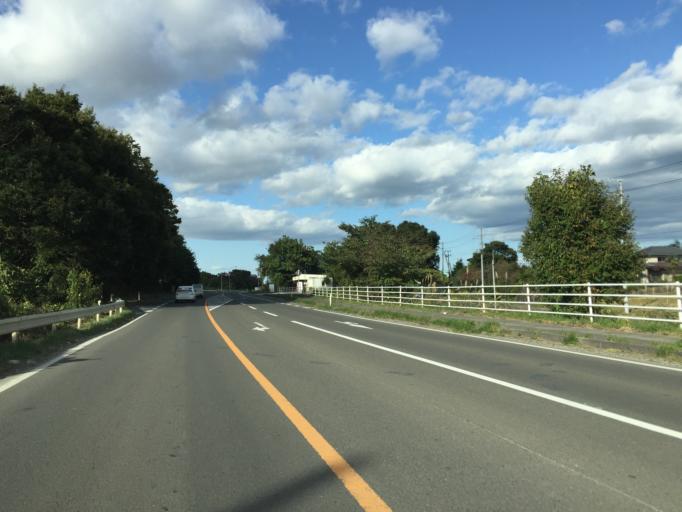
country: JP
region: Miyagi
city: Marumori
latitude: 37.9032
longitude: 140.9003
